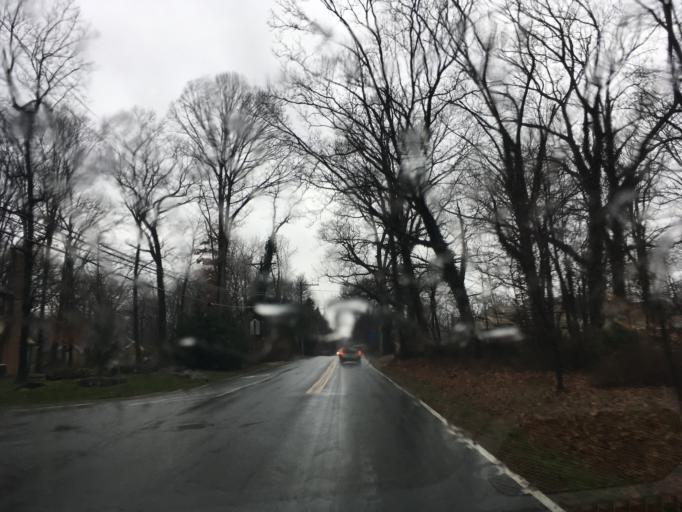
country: US
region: Delaware
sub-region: New Castle County
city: Bellefonte
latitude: 39.8189
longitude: -75.5137
